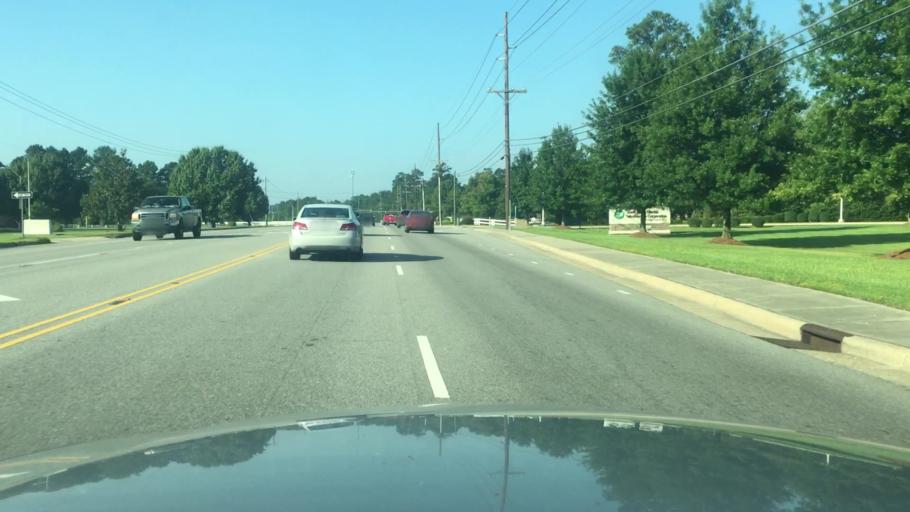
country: US
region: North Carolina
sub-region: Cumberland County
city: Eastover
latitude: 35.1636
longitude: -78.8656
